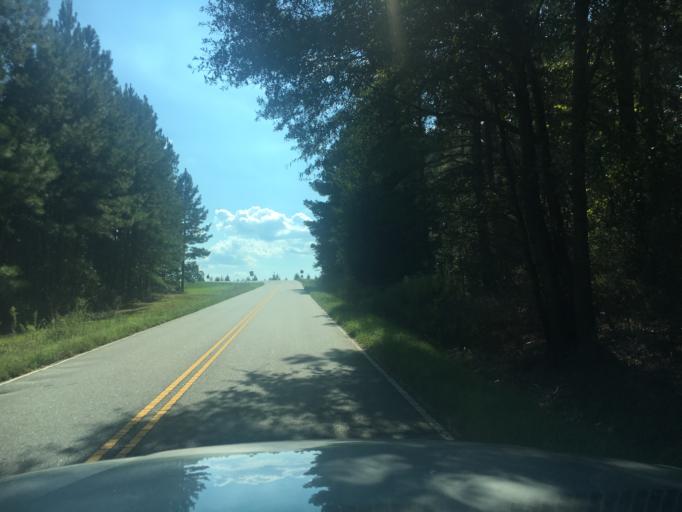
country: US
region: South Carolina
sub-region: Pickens County
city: Liberty
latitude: 34.7055
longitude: -82.6409
